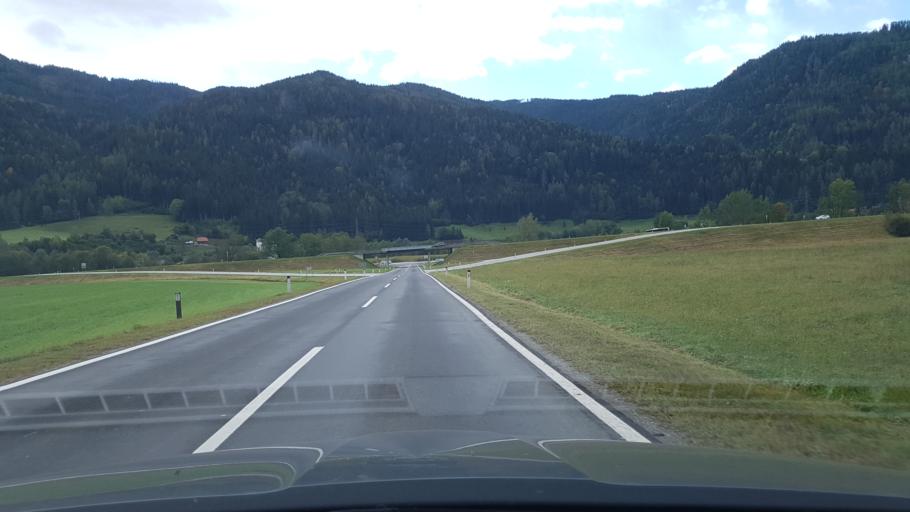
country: AT
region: Styria
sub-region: Politischer Bezirk Murau
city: Triebendorf
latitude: 47.1386
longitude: 14.2853
